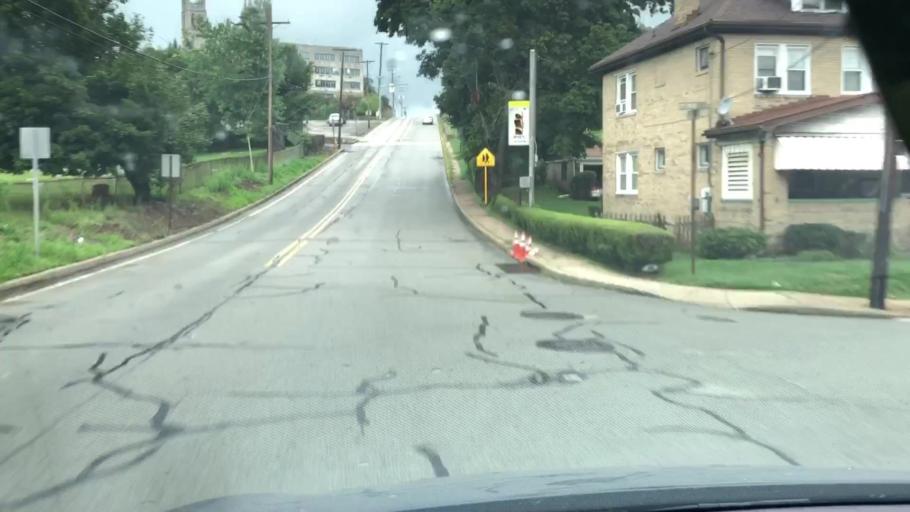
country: US
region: Pennsylvania
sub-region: Allegheny County
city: Dormont
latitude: 40.3859
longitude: -80.0409
